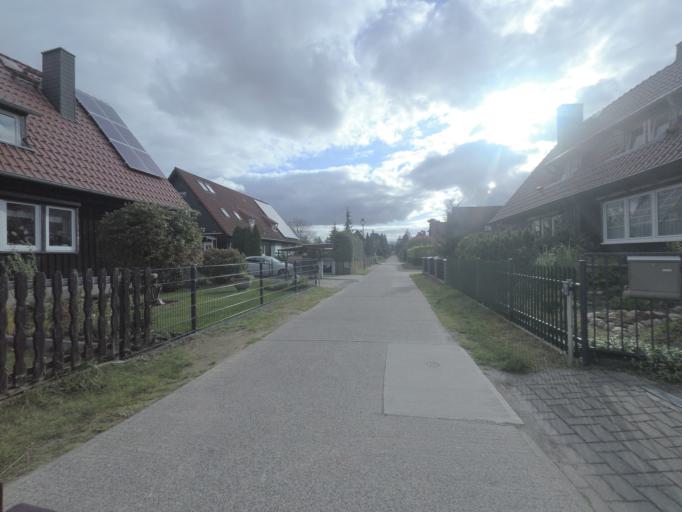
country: DE
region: Brandenburg
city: Ludwigsfelde
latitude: 52.3000
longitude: 13.2552
